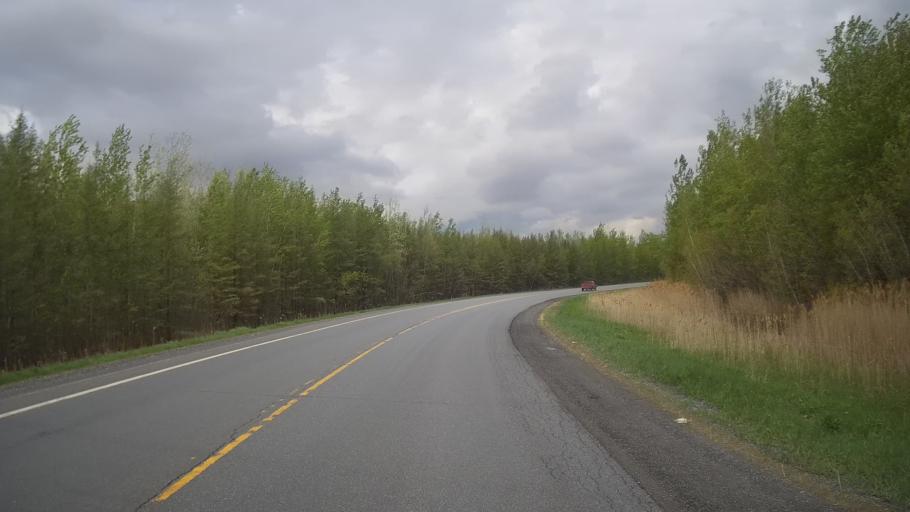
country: CA
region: Quebec
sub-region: Monteregie
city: Farnham
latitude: 45.2748
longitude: -72.9901
